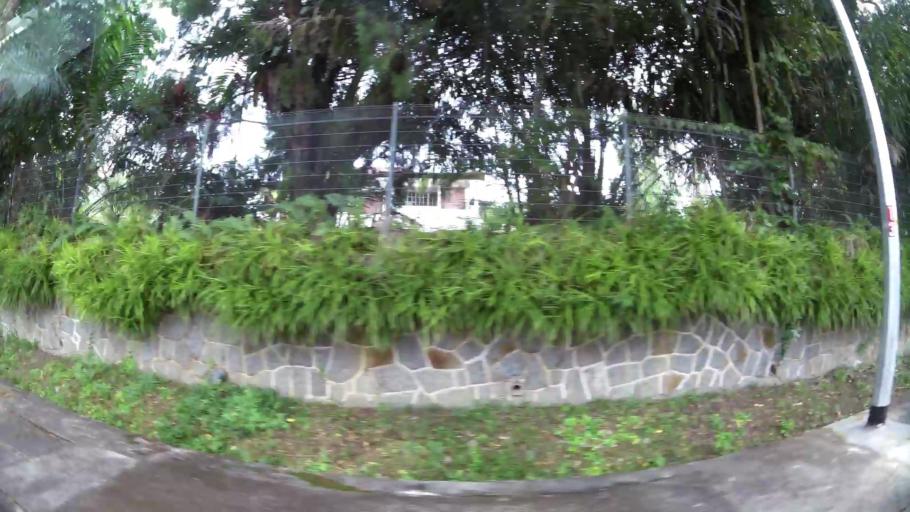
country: SG
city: Singapore
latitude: 1.3200
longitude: 103.7971
